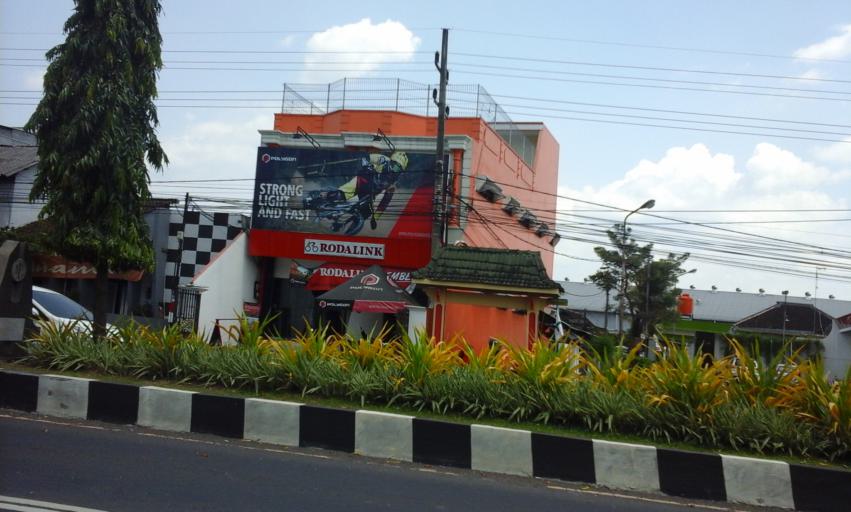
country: ID
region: East Java
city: Kaliwates
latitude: -8.1784
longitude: 113.6794
